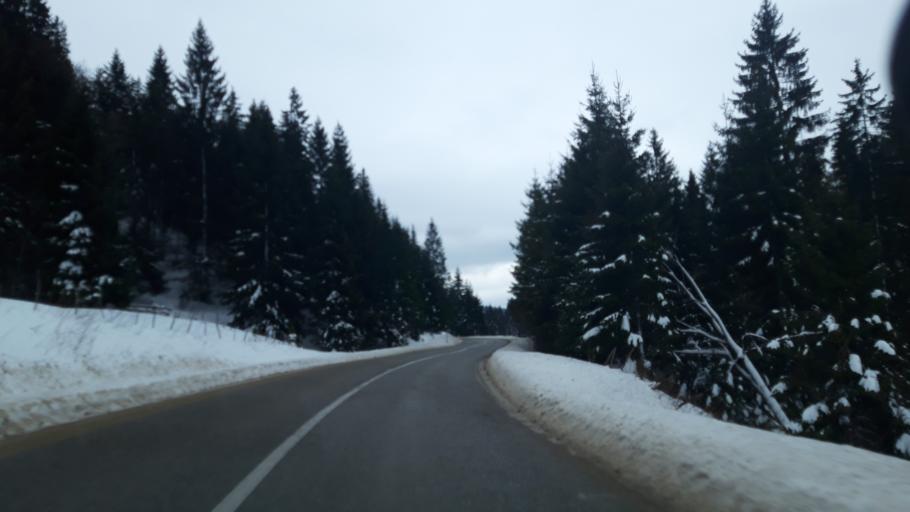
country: BA
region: Republika Srpska
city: Han Pijesak
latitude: 44.1203
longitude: 18.9692
